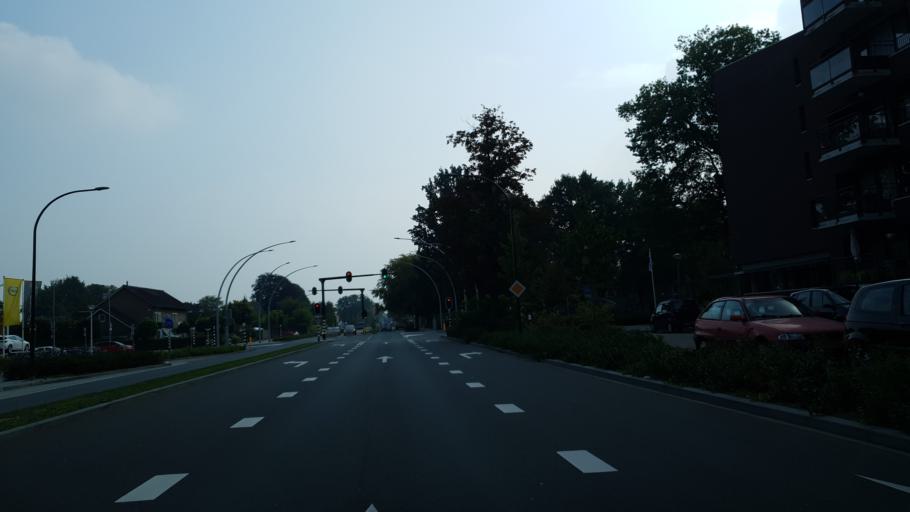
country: NL
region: North Brabant
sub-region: Gemeente Valkenswaard
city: Valkenswaard
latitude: 51.3555
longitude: 5.4641
